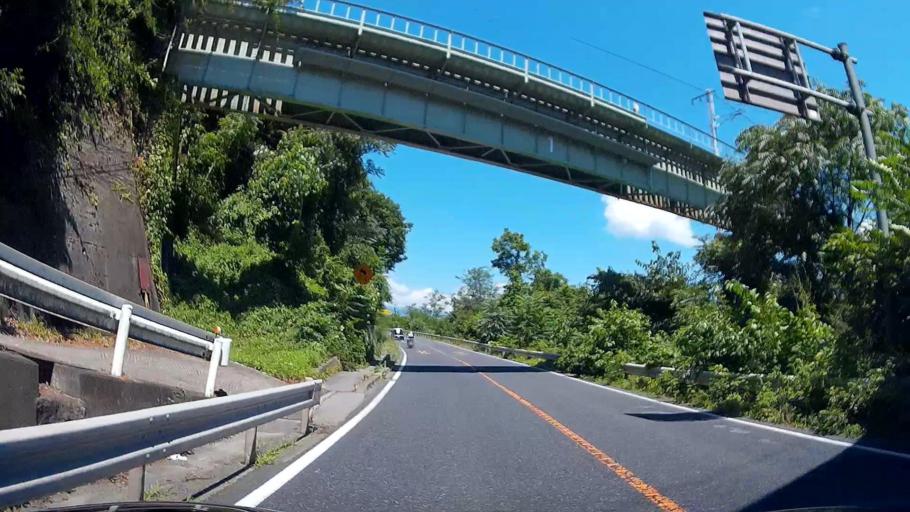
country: JP
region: Gunma
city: Numata
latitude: 36.6301
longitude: 139.0385
